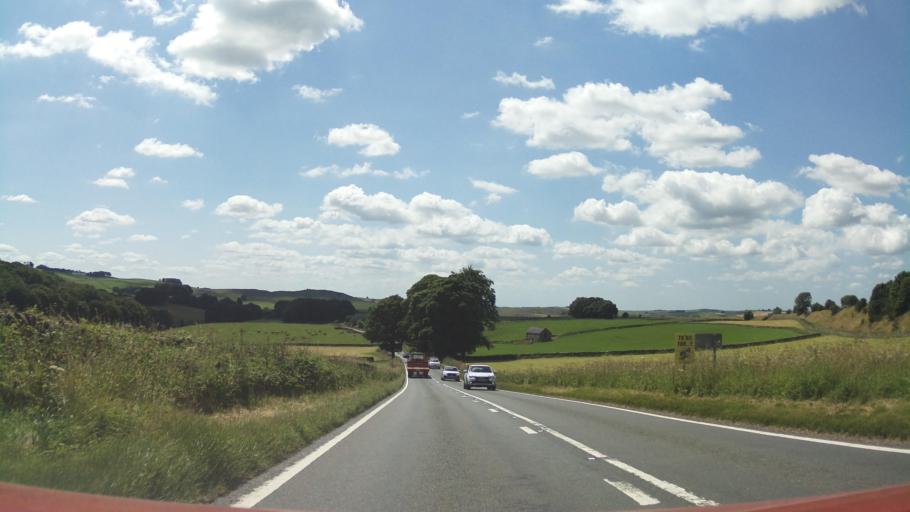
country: GB
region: England
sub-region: Derbyshire
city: Ashbourne
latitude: 53.1034
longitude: -1.7683
